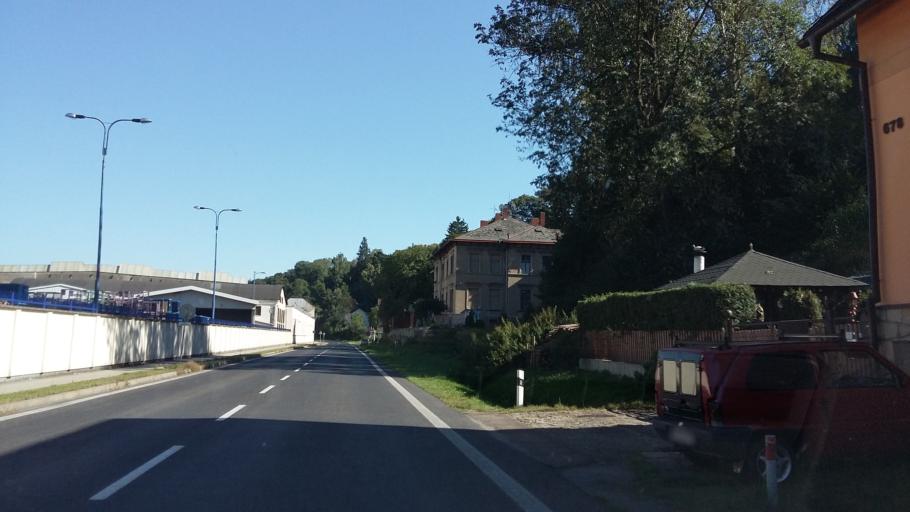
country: CZ
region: Central Bohemia
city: Bela pod Bezdezem
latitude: 50.4975
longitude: 14.8180
